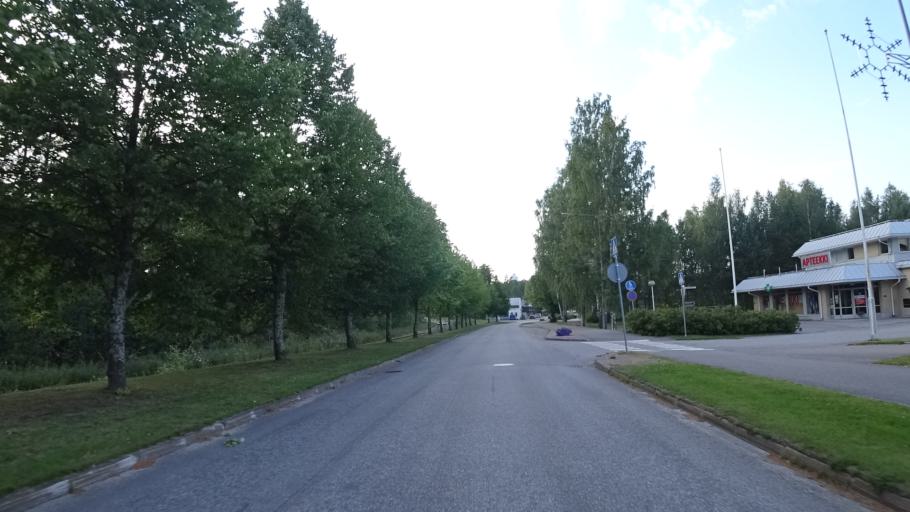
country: FI
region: Southern Savonia
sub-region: Savonlinna
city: Punkaharju
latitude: 61.7570
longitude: 29.3892
